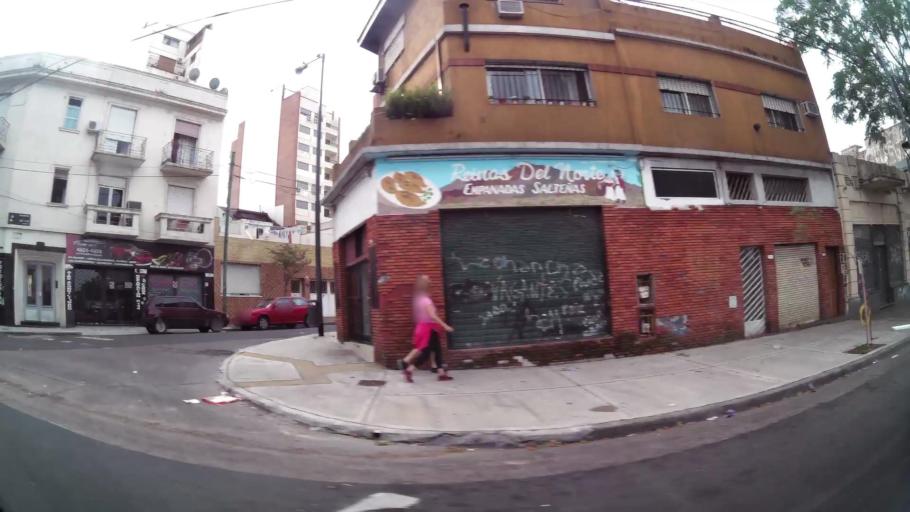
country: AR
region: Buenos Aires F.D.
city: Villa Santa Rita
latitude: -34.6334
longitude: -58.4320
